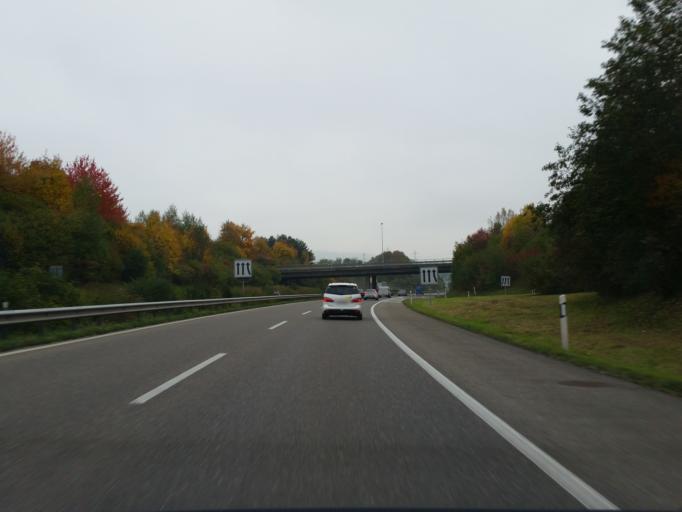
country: CH
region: Saint Gallen
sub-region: Wahlkreis Rorschach
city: Horn
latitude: 47.4807
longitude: 9.4435
